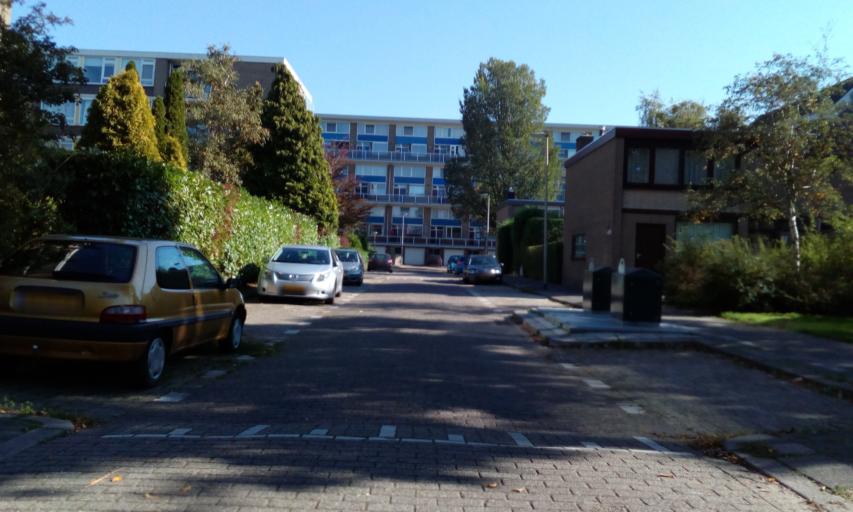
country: NL
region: South Holland
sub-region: Gemeente Vlaardingen
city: Vlaardingen
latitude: 51.9107
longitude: 4.3129
